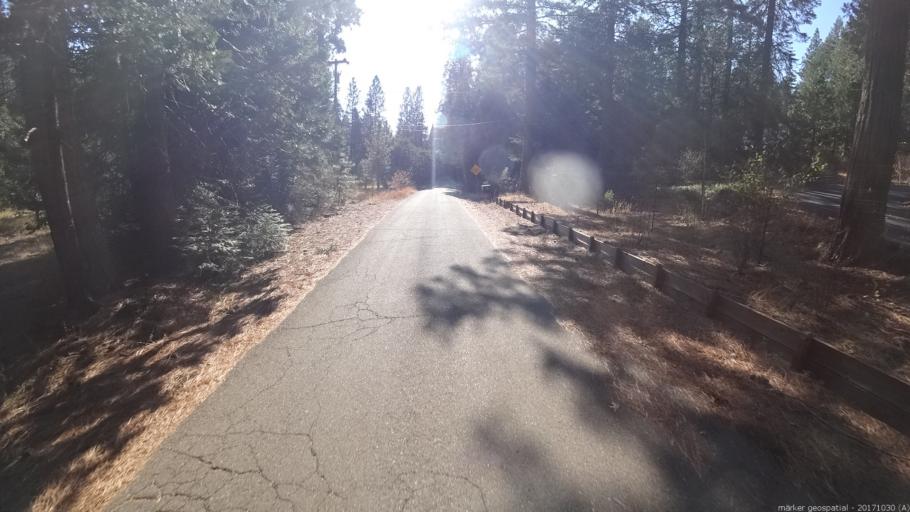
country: US
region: California
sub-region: Shasta County
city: Shingletown
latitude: 40.5039
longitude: -121.7412
